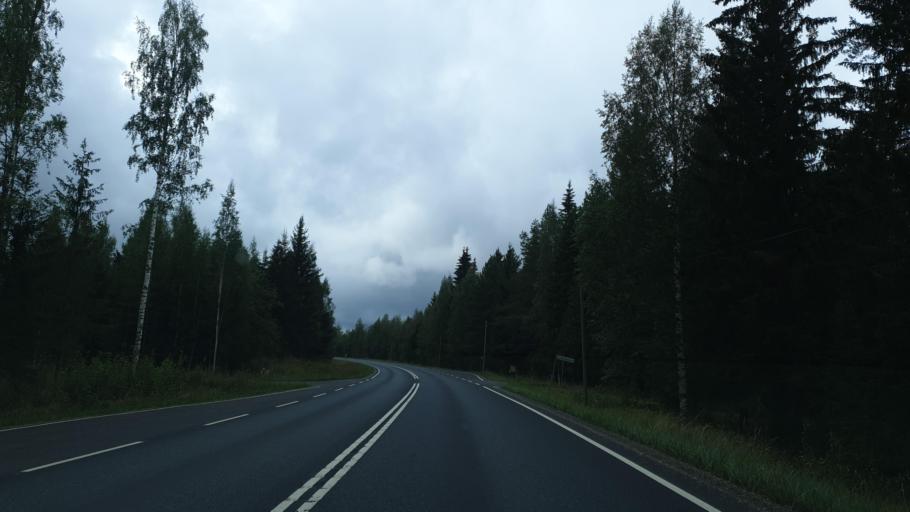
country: FI
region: Northern Savo
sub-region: Kuopio
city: Nilsiae
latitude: 63.2385
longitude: 28.2562
